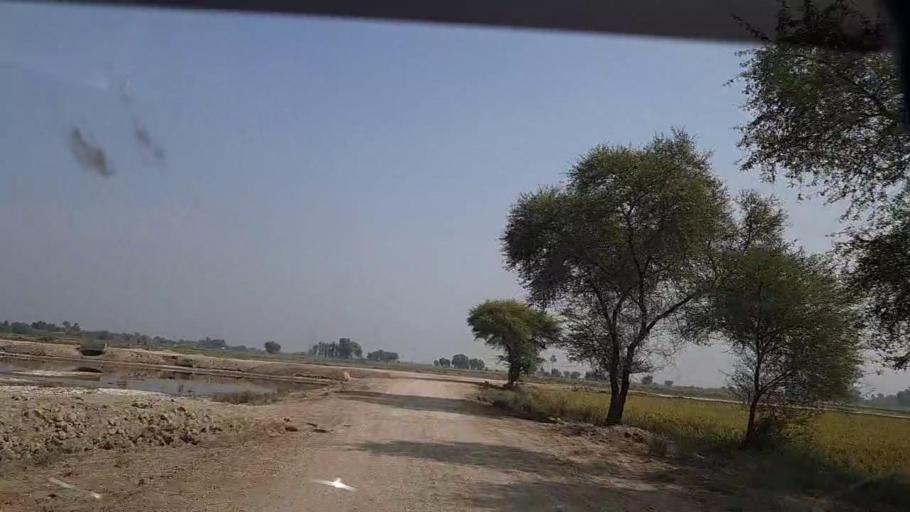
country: PK
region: Sindh
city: Shikarpur
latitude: 28.0513
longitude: 68.6685
